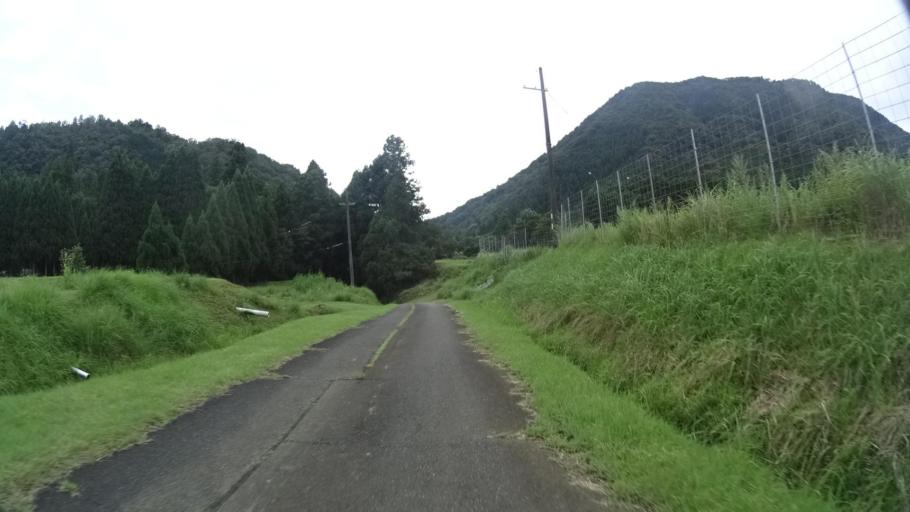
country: JP
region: Kyoto
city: Miyazu
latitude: 35.4365
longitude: 135.1510
